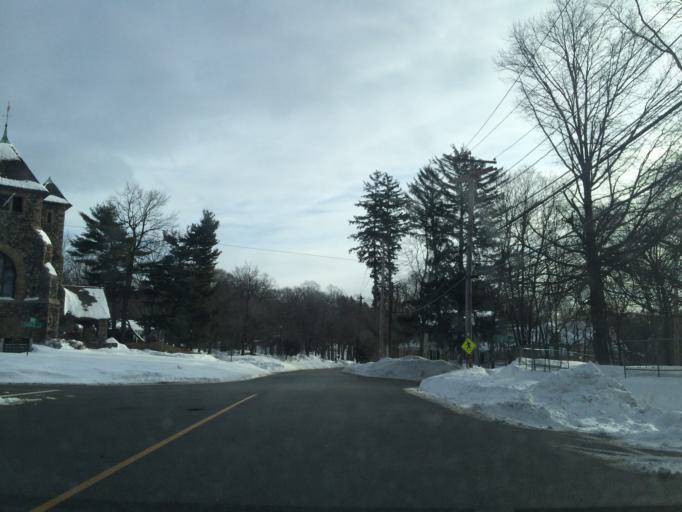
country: US
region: Massachusetts
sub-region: Middlesex County
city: Weston
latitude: 42.3680
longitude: -71.2980
